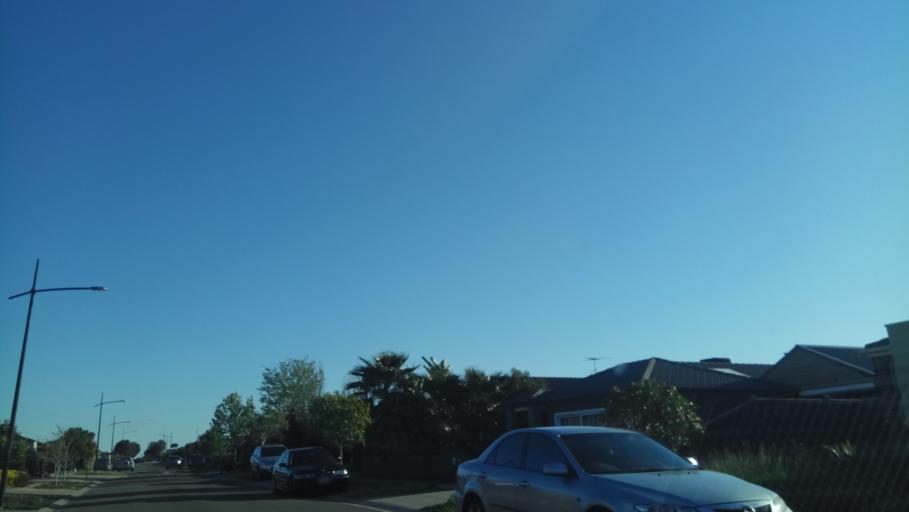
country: AU
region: Victoria
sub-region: Wyndham
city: Point Cook
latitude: -37.9029
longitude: 144.7454
